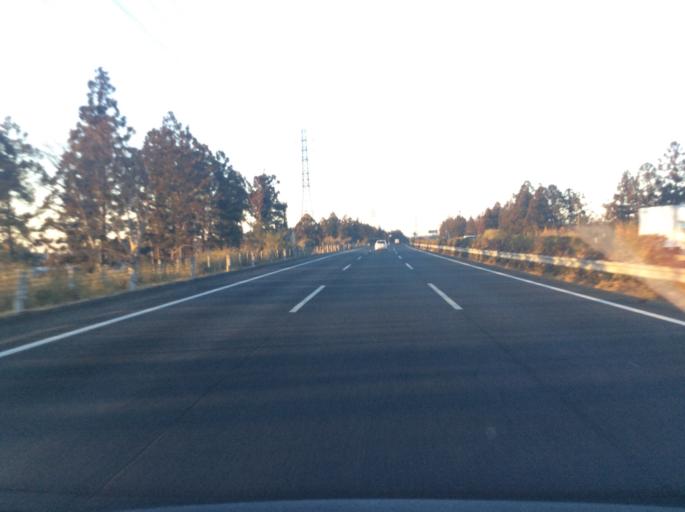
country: JP
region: Ibaraki
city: Mito-shi
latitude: 36.3672
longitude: 140.3813
